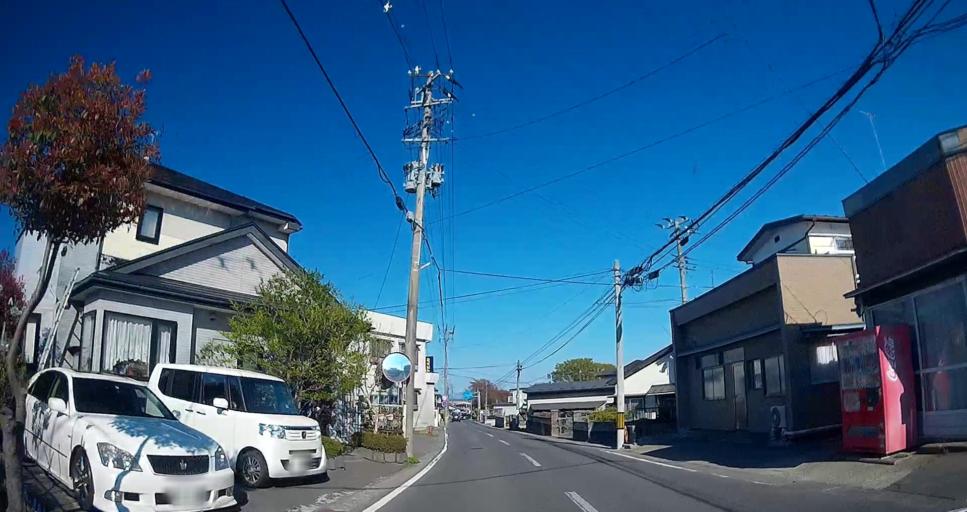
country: JP
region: Aomori
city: Hachinohe
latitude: 40.5241
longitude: 141.5538
